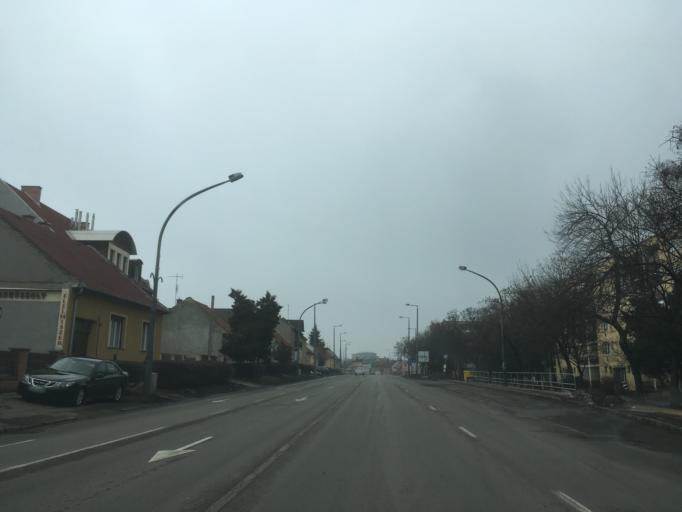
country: HU
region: Heves
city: Eger
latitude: 47.8877
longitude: 20.3806
